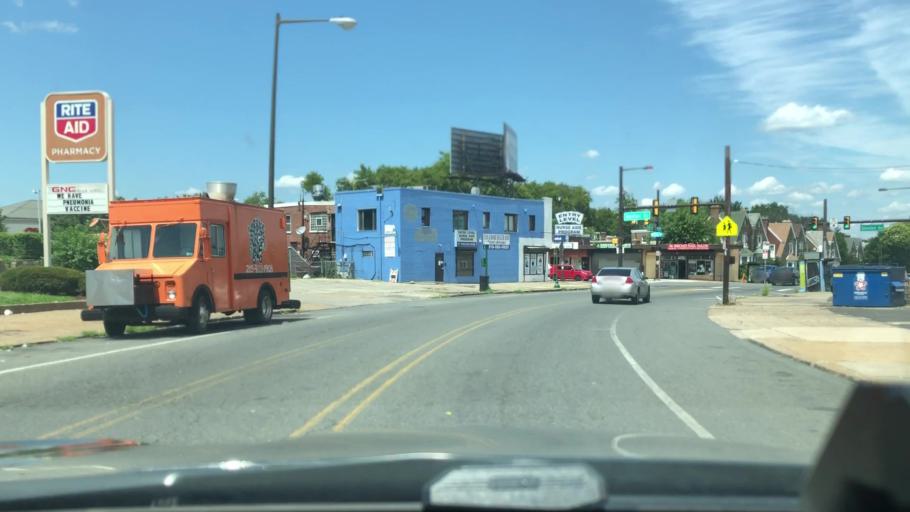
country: US
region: Pennsylvania
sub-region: Montgomery County
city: Wyndmoor
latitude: 40.0589
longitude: -75.1658
